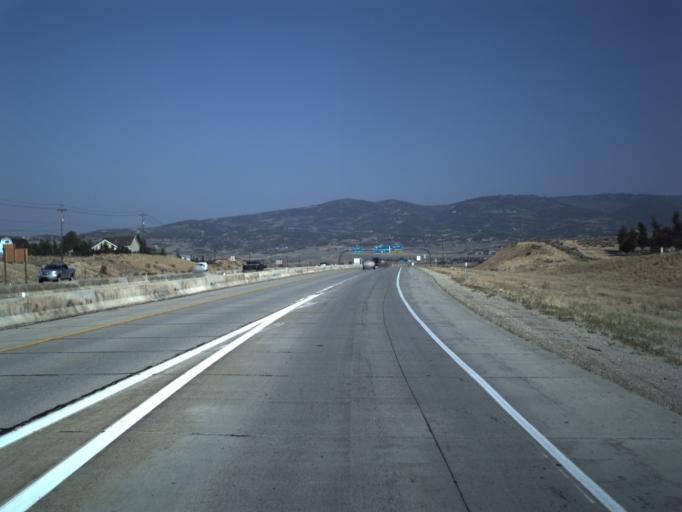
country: US
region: Utah
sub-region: Summit County
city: Snyderville
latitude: 40.7219
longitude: -111.4899
